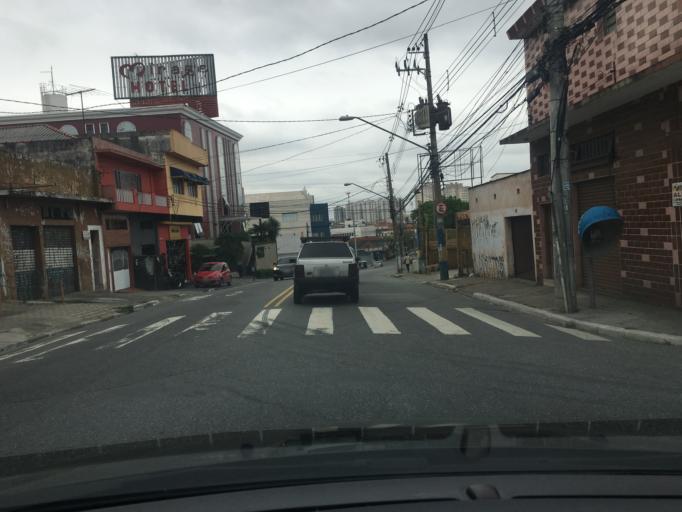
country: BR
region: Sao Paulo
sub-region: Guarulhos
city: Guarulhos
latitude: -23.4969
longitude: -46.5499
